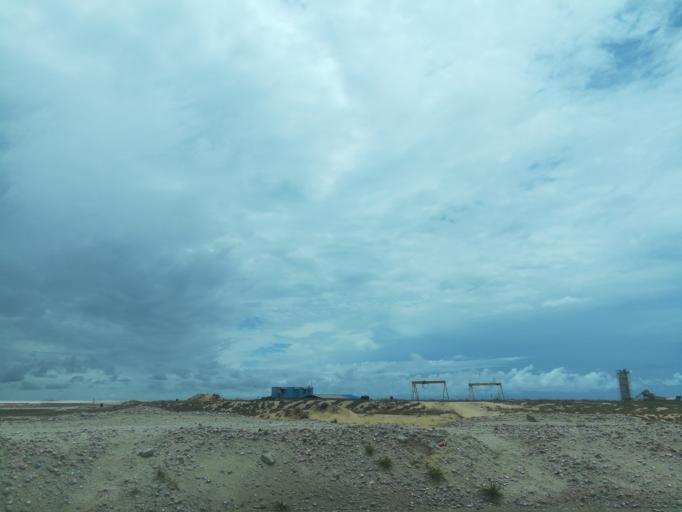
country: NG
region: Lagos
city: Ikoyi
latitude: 6.4120
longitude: 3.4263
